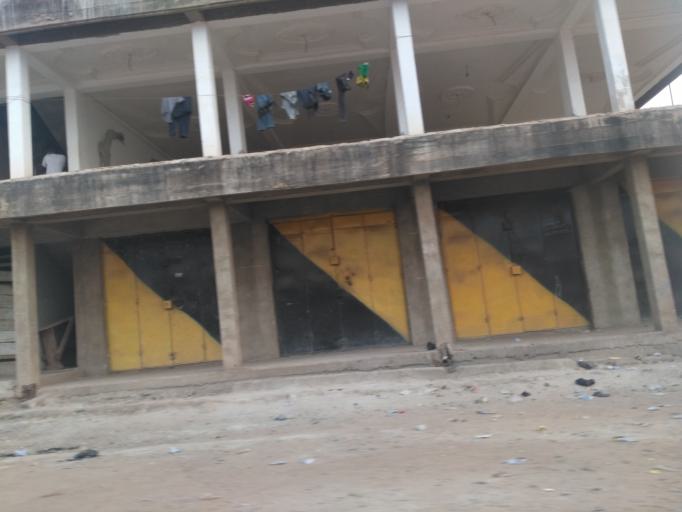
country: GH
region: Ashanti
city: Kumasi
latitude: 6.6808
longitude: -1.6145
